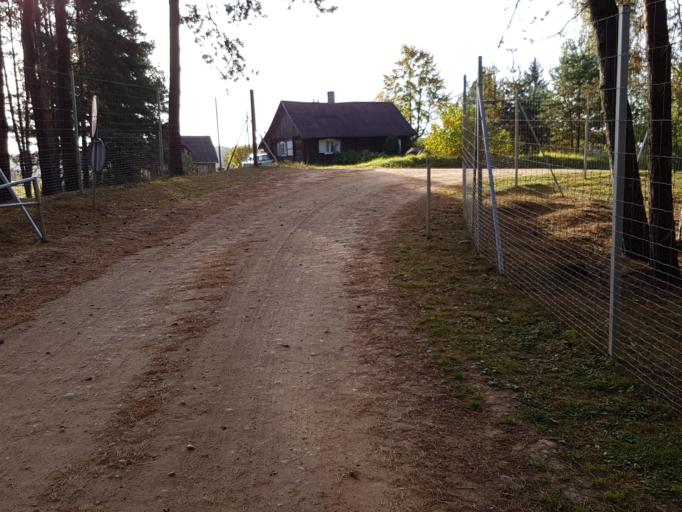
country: LT
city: Moletai
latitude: 55.0387
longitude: 25.4167
